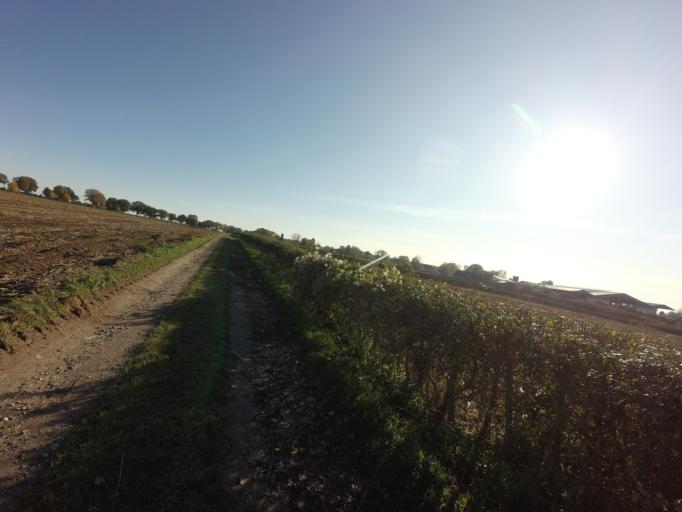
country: NL
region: Limburg
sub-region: Gemeente Simpelveld
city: Simpelveld
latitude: 50.8220
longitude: 5.9751
